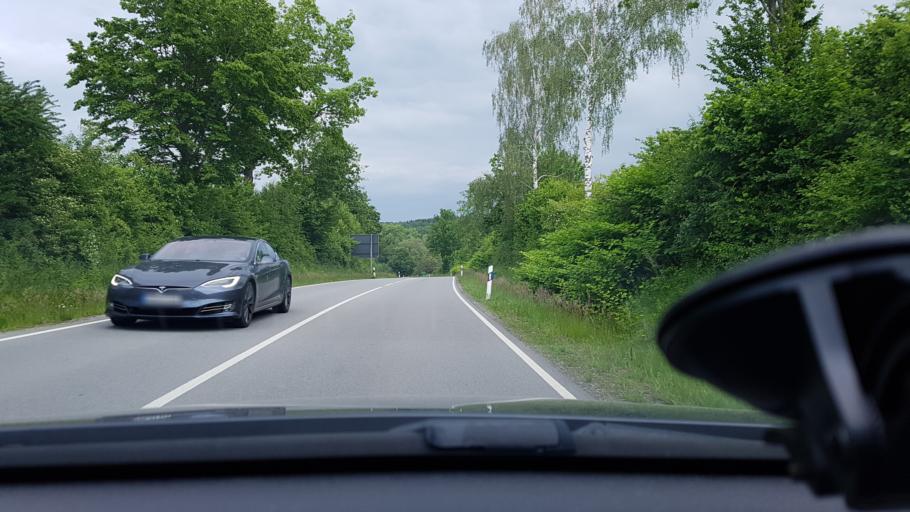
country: DE
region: Bavaria
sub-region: Lower Bavaria
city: Pfarrkirchen
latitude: 48.4182
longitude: 12.9528
